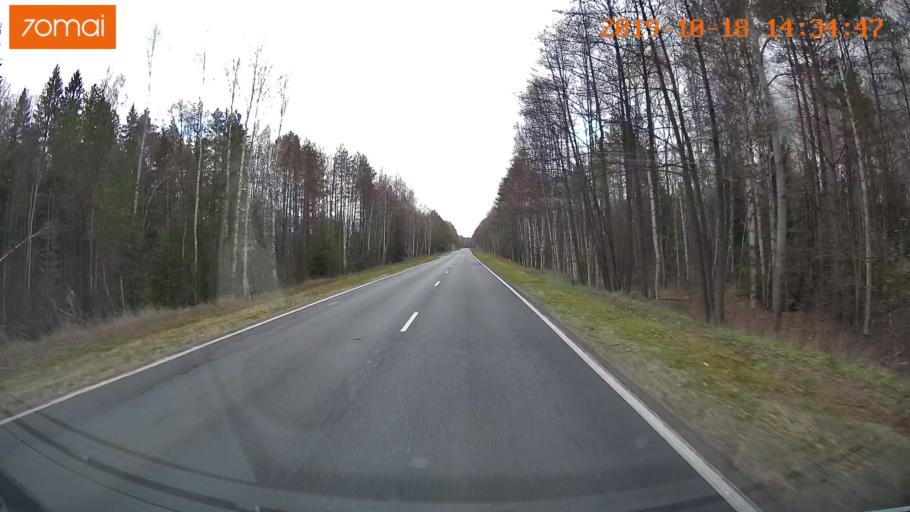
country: RU
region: Vladimir
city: Velikodvorskiy
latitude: 55.2159
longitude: 40.6229
